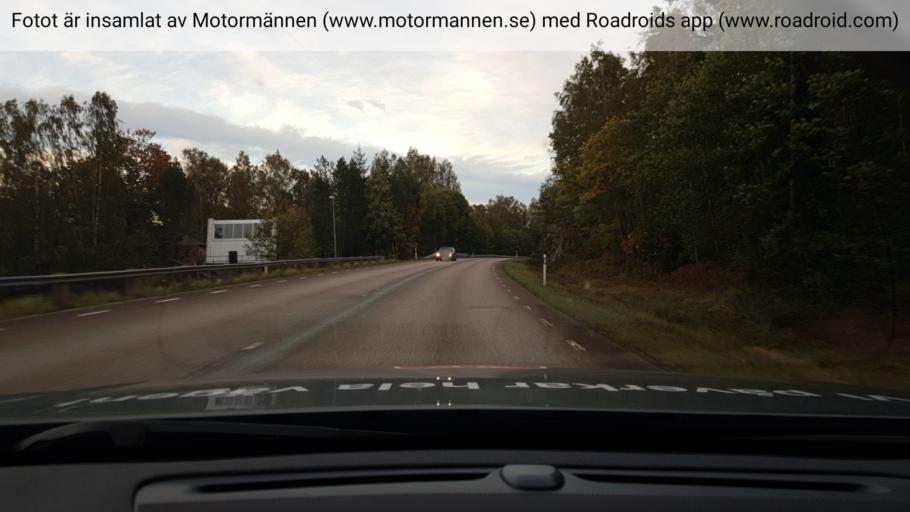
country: SE
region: Vaestra Goetaland
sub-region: Amals Kommun
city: Amal
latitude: 59.0793
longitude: 12.6058
